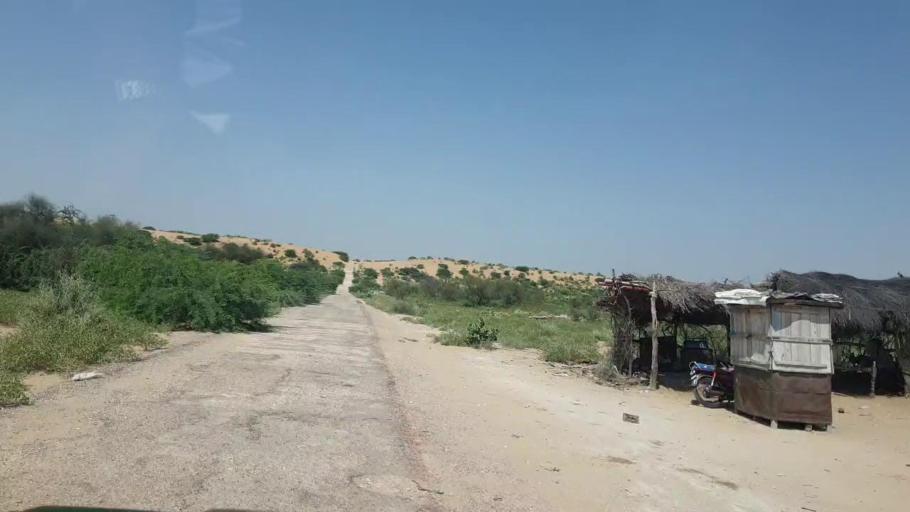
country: PK
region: Sindh
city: Chor
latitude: 25.3481
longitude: 70.3480
